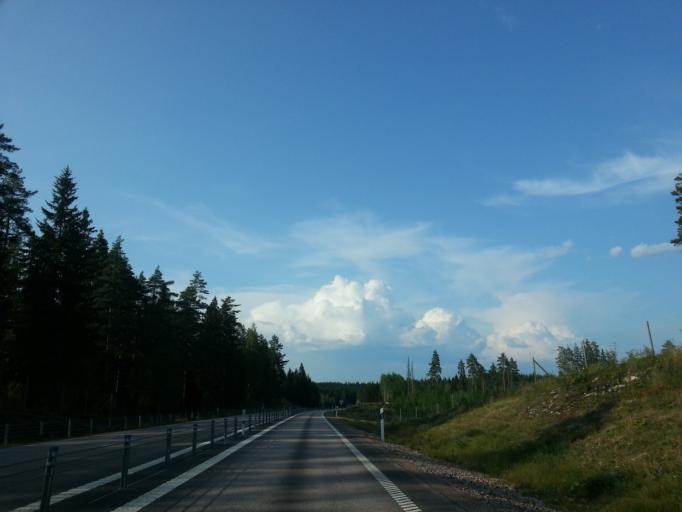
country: SE
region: Vaestmanland
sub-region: Norbergs Kommun
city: Norberg
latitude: 60.0871
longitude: 15.9871
